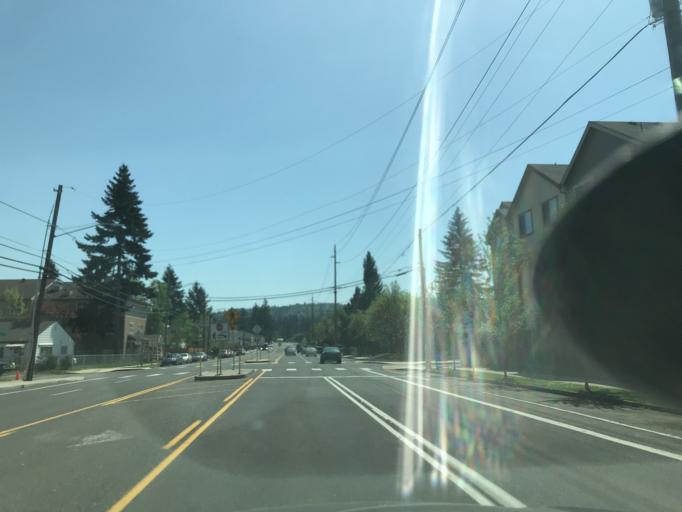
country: US
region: Oregon
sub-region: Multnomah County
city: Lents
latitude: 45.4879
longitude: -122.5378
